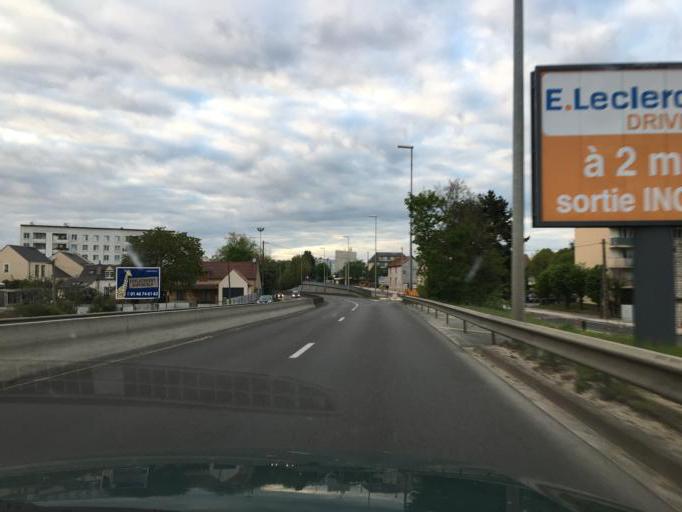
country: FR
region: Centre
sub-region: Departement du Loiret
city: Saint-Jean-de-la-Ruelle
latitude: 47.9032
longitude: 1.8721
